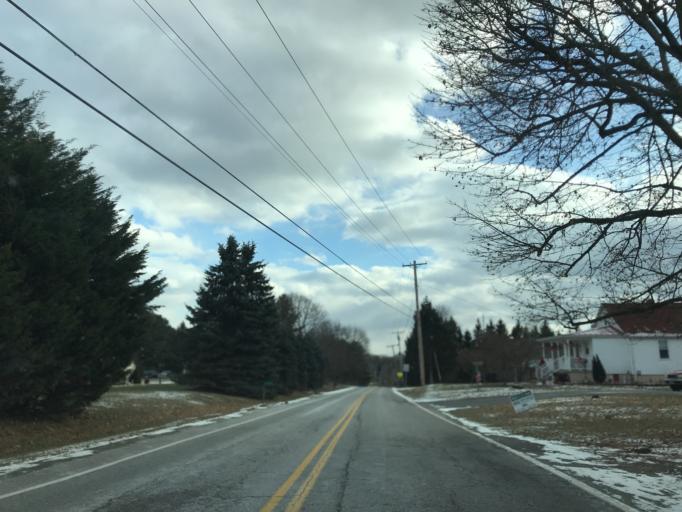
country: US
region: Maryland
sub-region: Harford County
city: Jarrettsville
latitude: 39.6205
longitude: -76.4528
